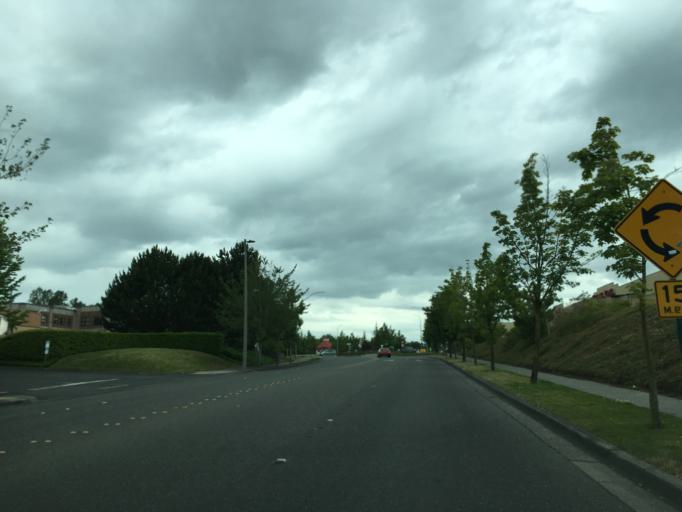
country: US
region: Washington
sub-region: Whatcom County
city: Bellingham
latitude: 48.7905
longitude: -122.4913
